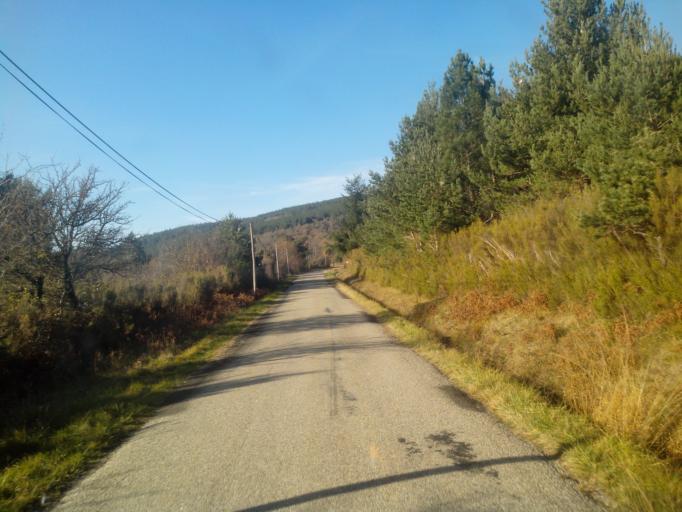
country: FR
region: Languedoc-Roussillon
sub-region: Departement des Pyrenees-Orientales
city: Saint-Paul-de-Fenouillet
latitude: 42.8654
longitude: 2.4236
